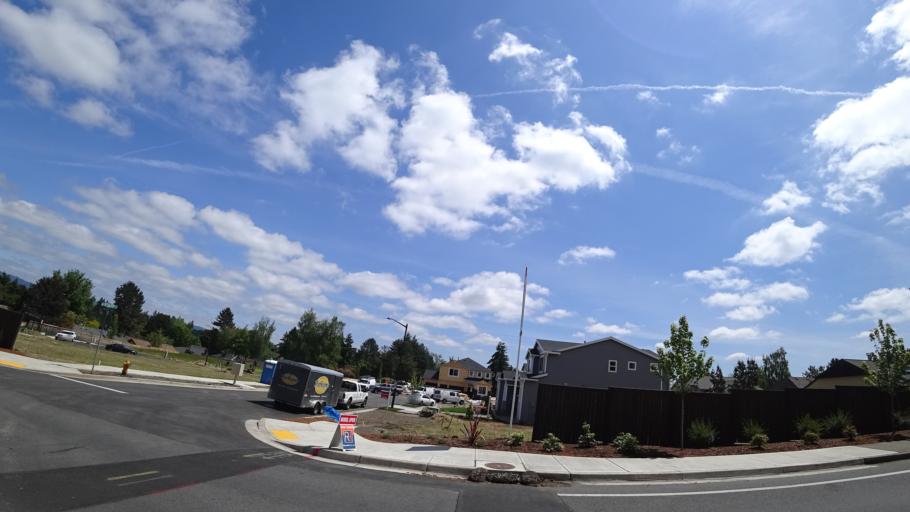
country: US
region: Oregon
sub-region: Washington County
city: King City
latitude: 45.4327
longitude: -122.8158
